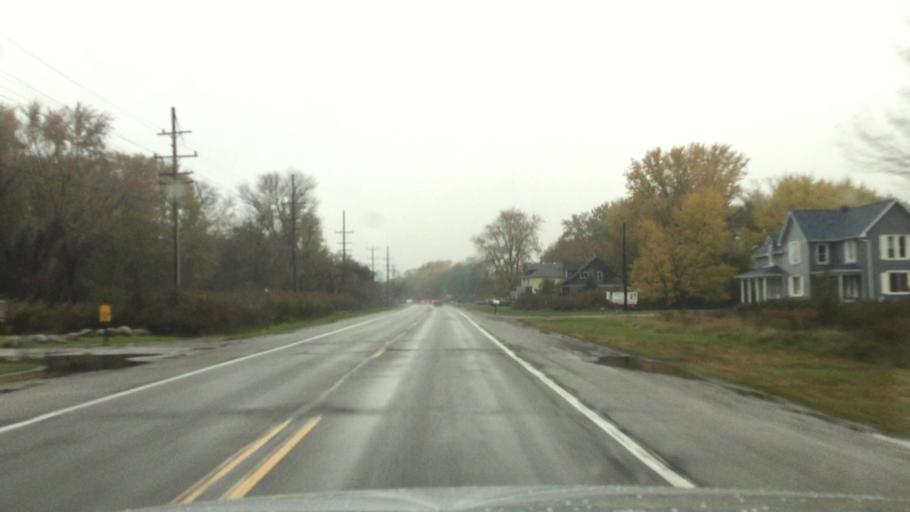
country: US
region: Michigan
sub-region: Saint Clair County
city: Pearl Beach
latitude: 42.6755
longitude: -82.6319
